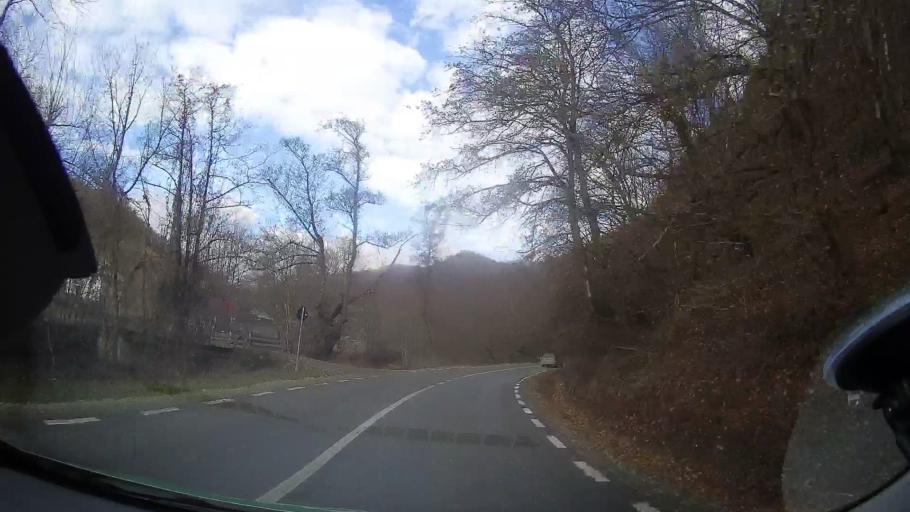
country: RO
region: Cluj
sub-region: Comuna Baisoara
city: Baisoara
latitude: 46.6029
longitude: 23.4248
